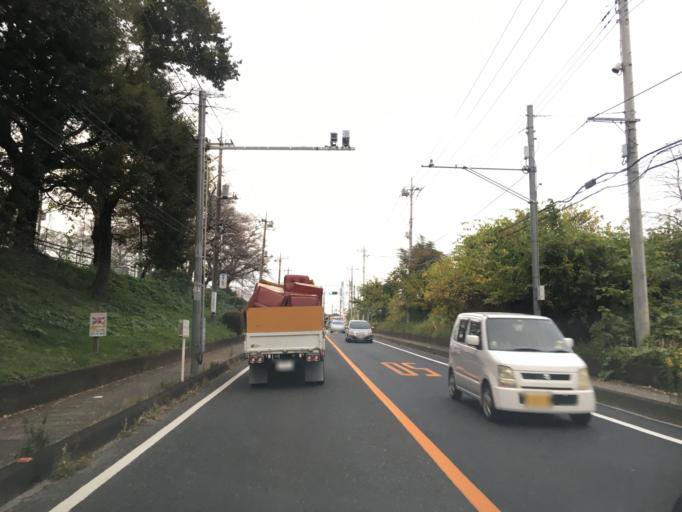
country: JP
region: Saitama
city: Sayama
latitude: 35.8602
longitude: 139.3798
